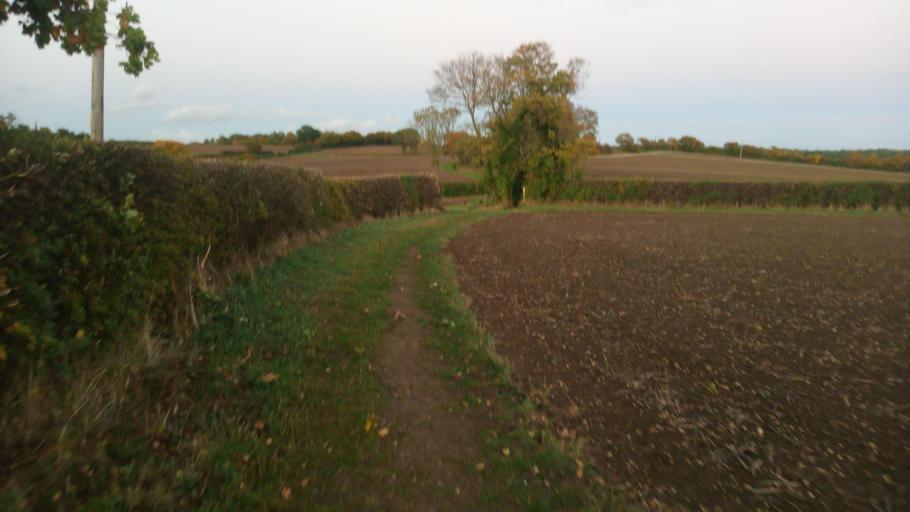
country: GB
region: England
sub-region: Cambridgeshire
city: Linton
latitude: 52.0558
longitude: 0.3186
